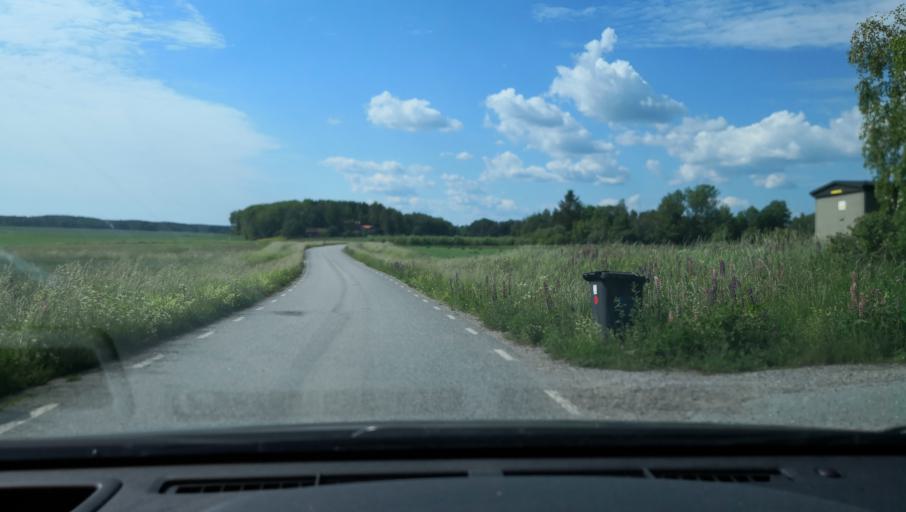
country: SE
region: Uppsala
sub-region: Enkopings Kommun
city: Orsundsbro
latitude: 59.8196
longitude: 17.3298
